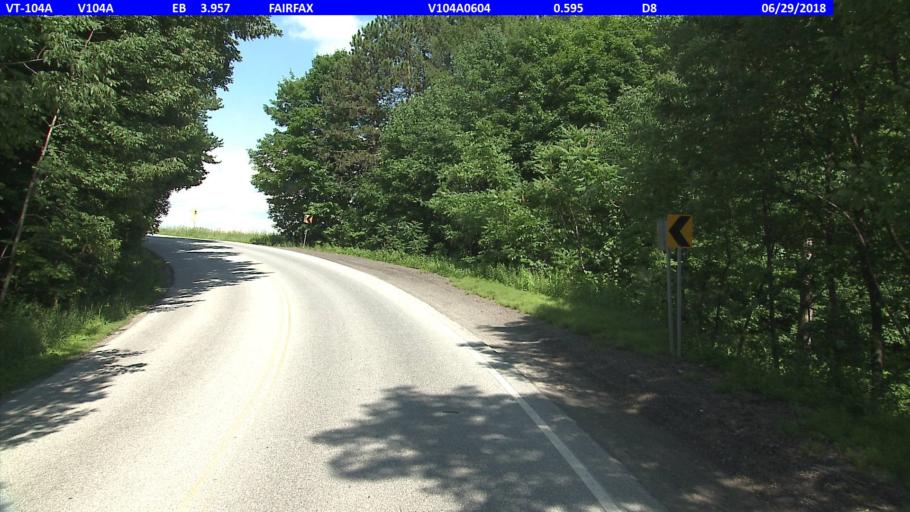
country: US
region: Vermont
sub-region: Chittenden County
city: Milton
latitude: 44.6805
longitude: -73.0395
